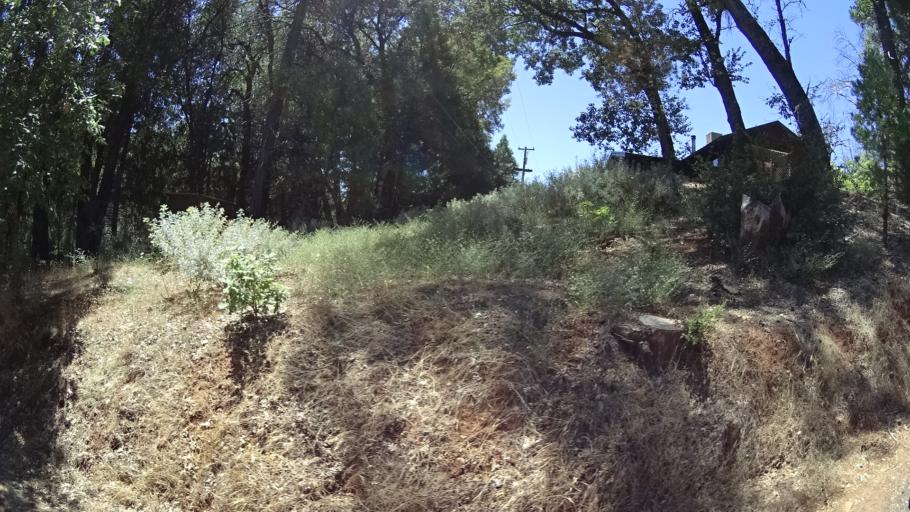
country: US
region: California
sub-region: Calaveras County
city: Mountain Ranch
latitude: 38.2753
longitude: -120.5921
